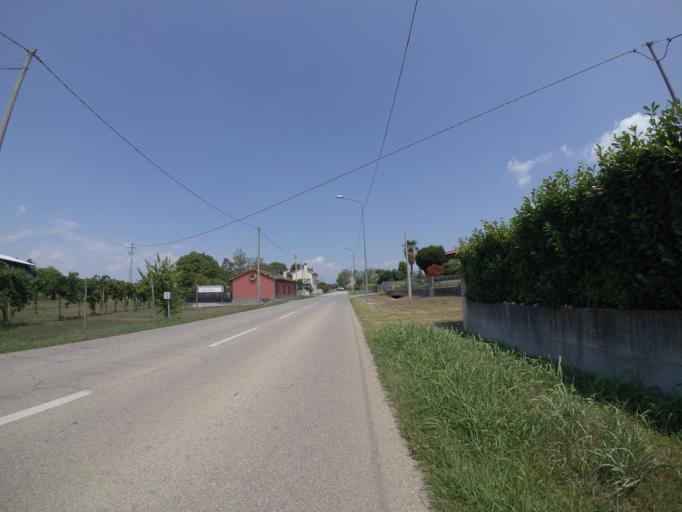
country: IT
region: Friuli Venezia Giulia
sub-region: Provincia di Udine
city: Sedegliano
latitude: 45.9930
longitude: 12.9690
